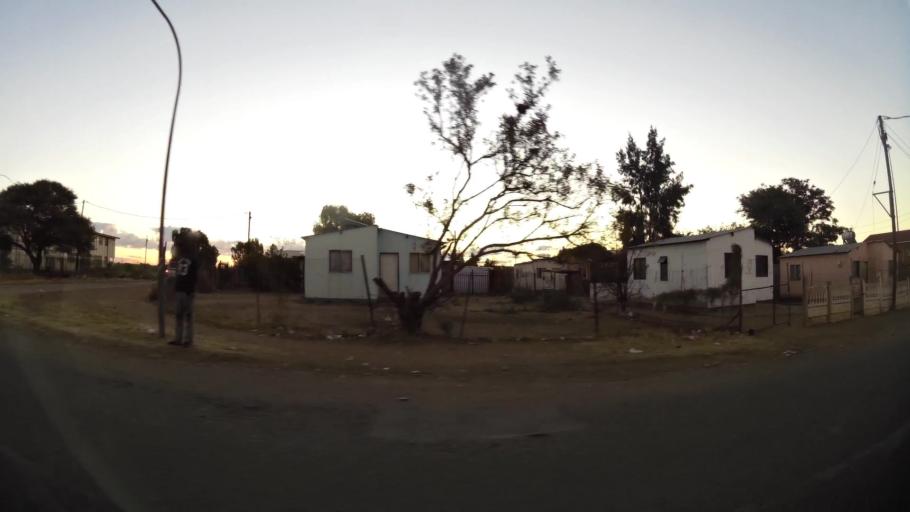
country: ZA
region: Northern Cape
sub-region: Frances Baard District Municipality
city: Kimberley
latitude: -28.7160
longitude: 24.7676
